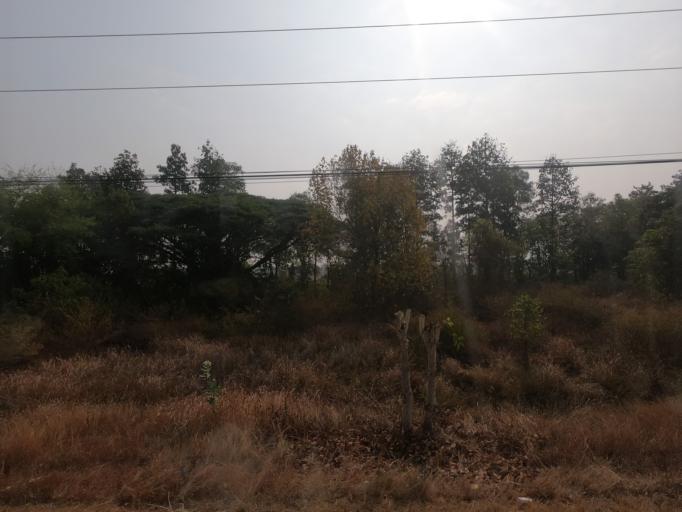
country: TH
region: Khon Kaen
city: Ban Haet
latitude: 16.1334
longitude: 102.7464
